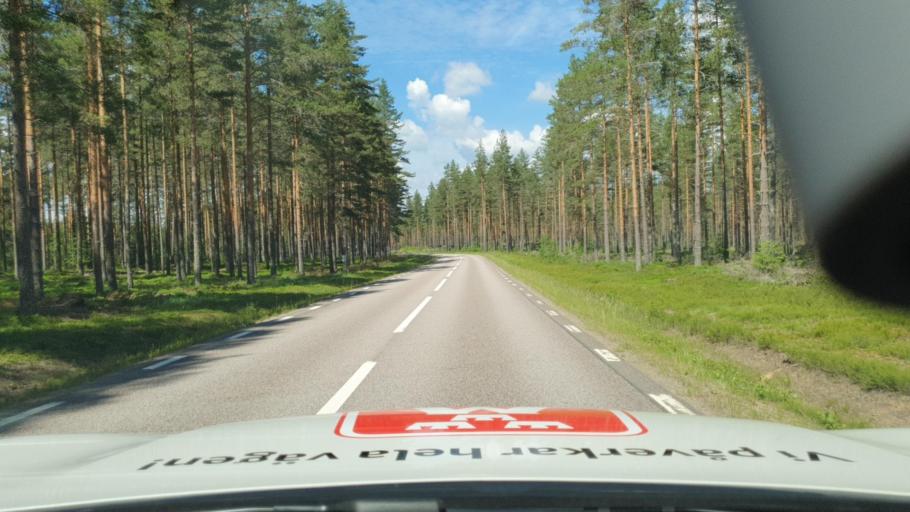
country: SE
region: Vaermland
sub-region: Torsby Kommun
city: Torsby
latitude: 60.3689
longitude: 12.9291
